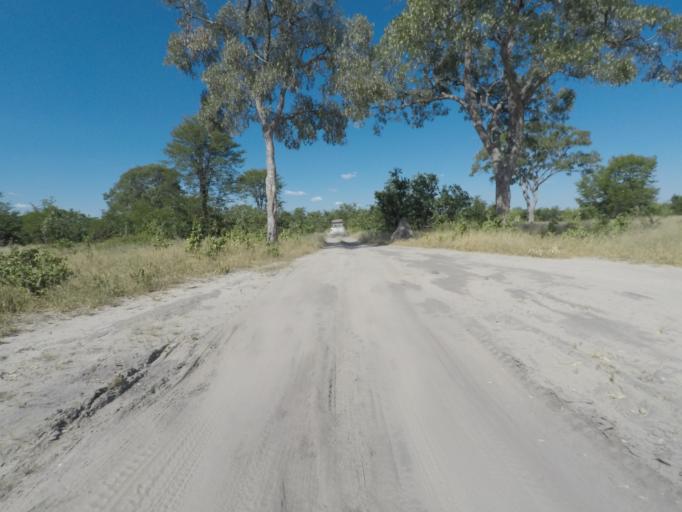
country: BW
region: North West
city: Maun
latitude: -19.4256
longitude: 23.6349
